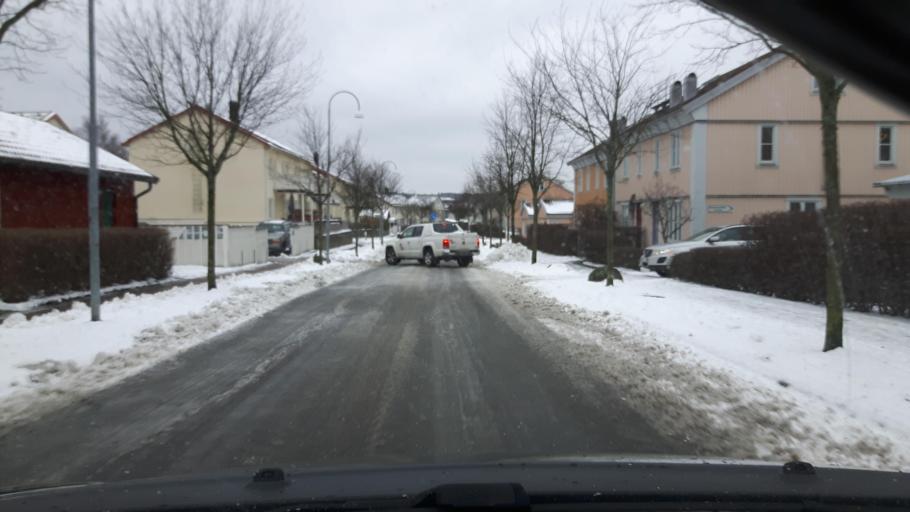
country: SE
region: Vaestra Goetaland
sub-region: Molndal
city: Moelndal
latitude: 57.6537
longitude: 11.9626
